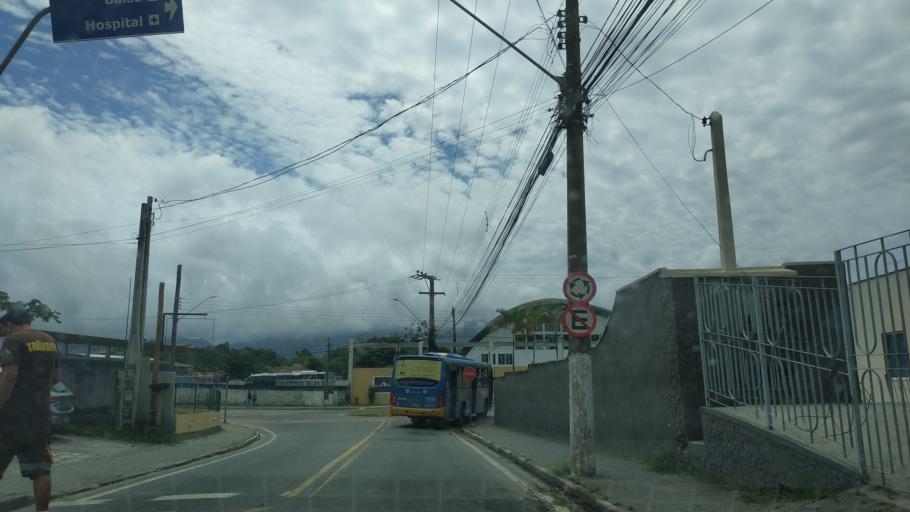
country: BR
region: Sao Paulo
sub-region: Ilhabela
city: Ilhabela
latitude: -23.8242
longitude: -45.3664
